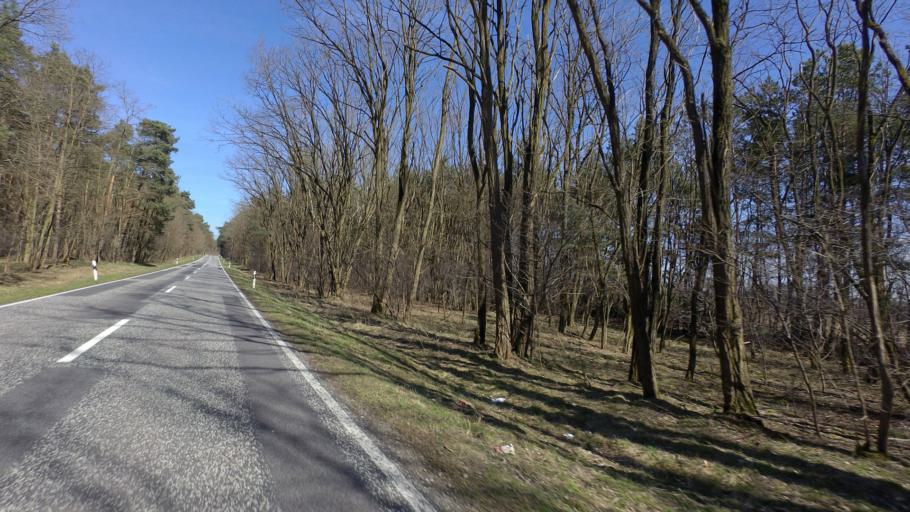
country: DE
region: Brandenburg
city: Waldsieversdorf
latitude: 52.4768
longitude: 14.0682
